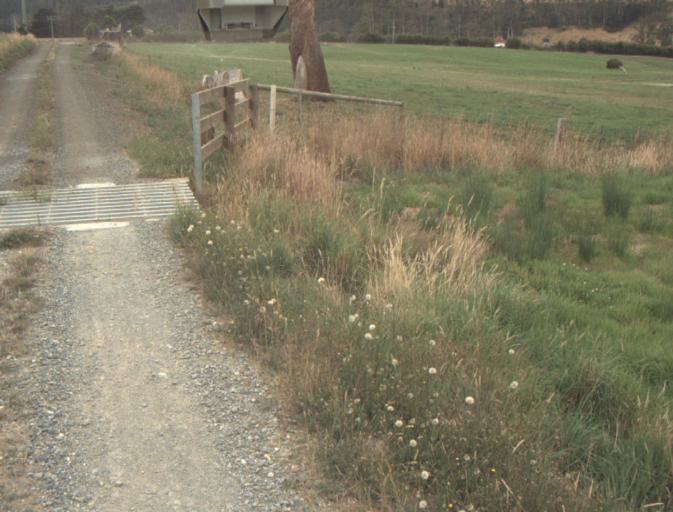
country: AU
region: Tasmania
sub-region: Launceston
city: Mayfield
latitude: -41.2404
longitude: 147.2061
